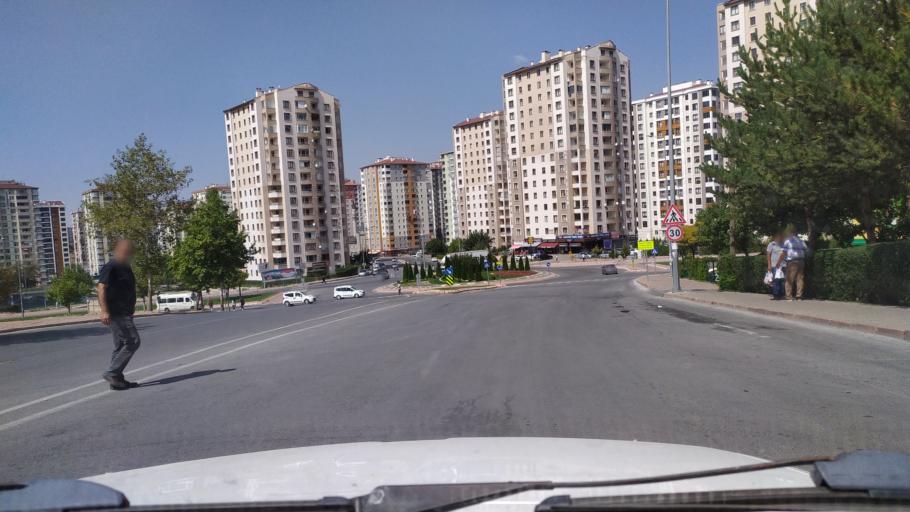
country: TR
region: Kayseri
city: Talas
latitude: 38.7076
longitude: 35.5608
